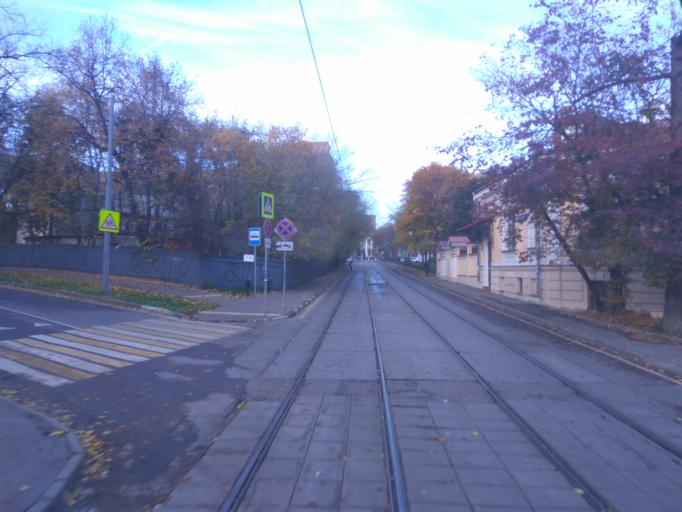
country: RU
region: Moscow
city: Mar'ina Roshcha
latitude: 55.7811
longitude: 37.6090
